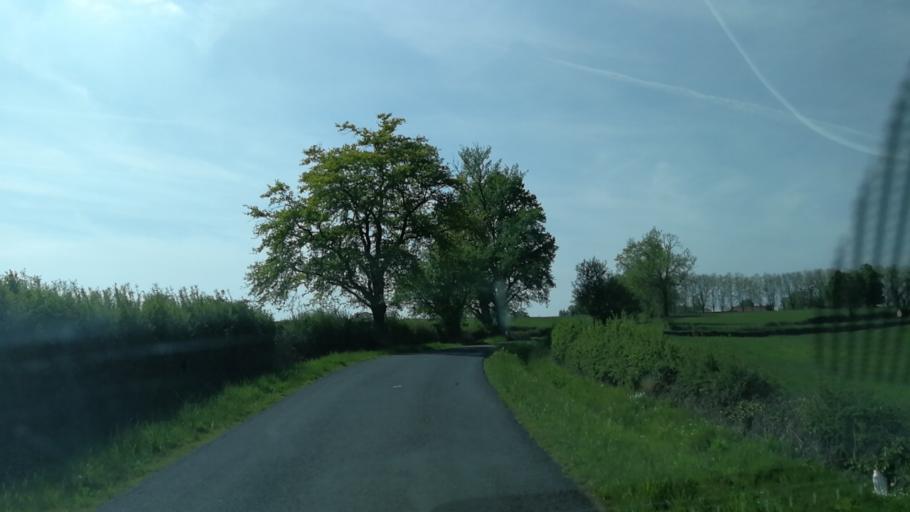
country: FR
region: Auvergne
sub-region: Departement de l'Allier
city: Saint-Gerand-le-Puy
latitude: 46.3877
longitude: 3.5821
